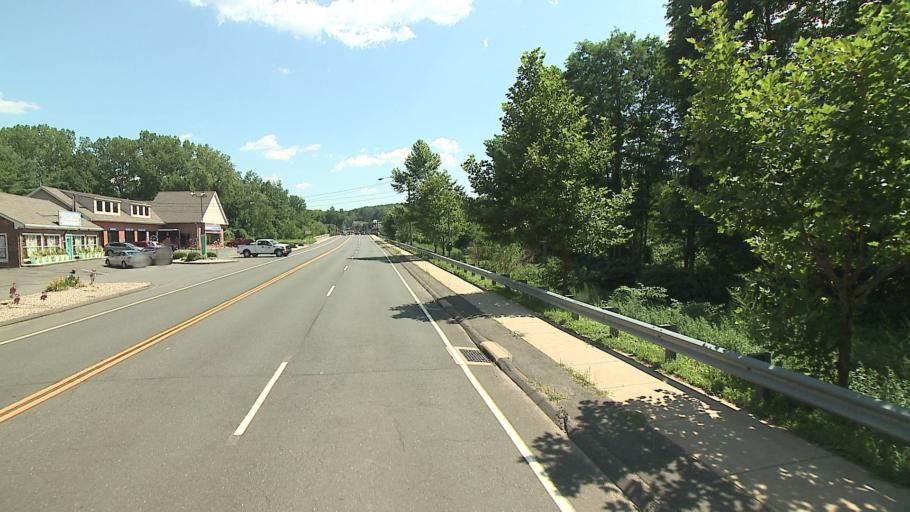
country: US
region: Connecticut
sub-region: Hartford County
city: Farmington
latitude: 41.7302
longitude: -72.8303
